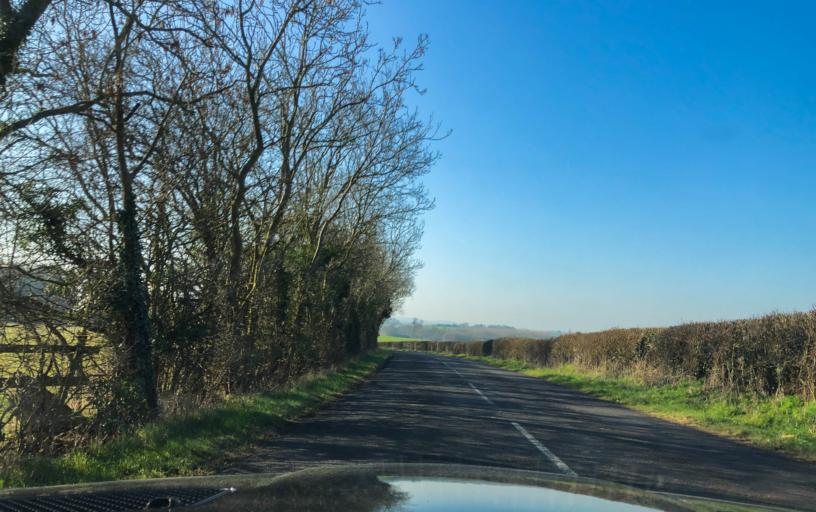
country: GB
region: England
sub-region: Warwickshire
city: Wellesbourne Mountford
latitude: 52.2230
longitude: -1.5656
